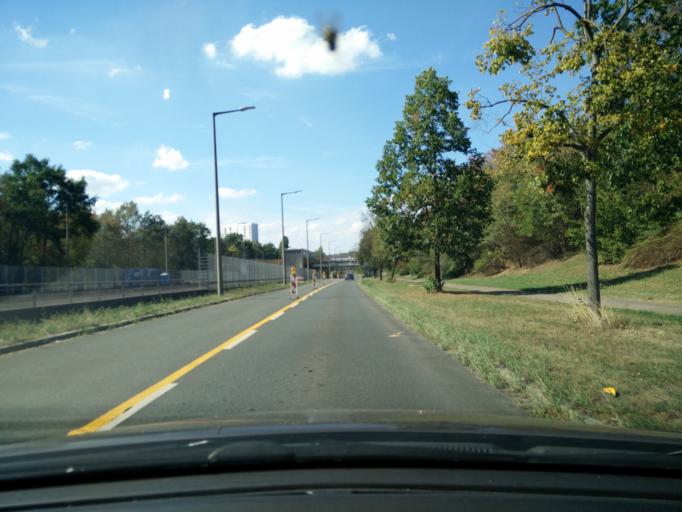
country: DE
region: Bavaria
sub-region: Regierungsbezirk Mittelfranken
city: Nuernberg
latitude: 49.4109
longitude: 11.1237
